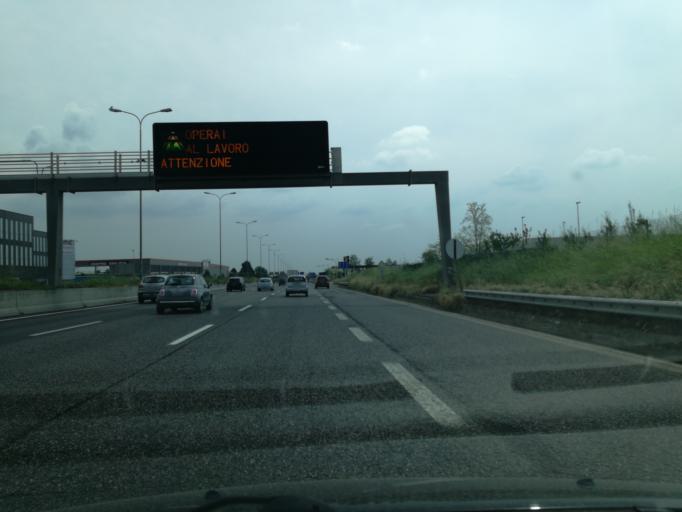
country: IT
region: Lombardy
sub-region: Provincia di Monza e Brianza
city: Verano Brianza
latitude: 45.6739
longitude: 9.2195
